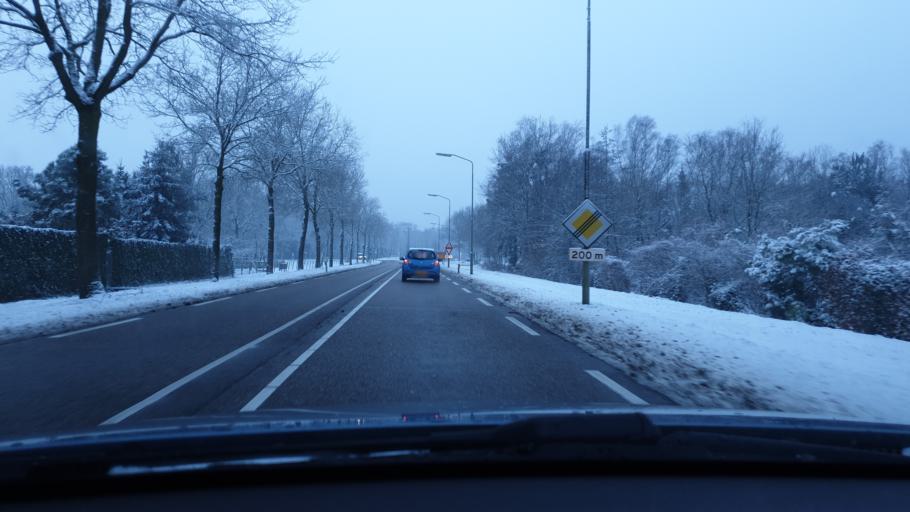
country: NL
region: North Brabant
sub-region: Gemeente Landerd
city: Zeeland
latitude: 51.6895
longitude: 5.6622
